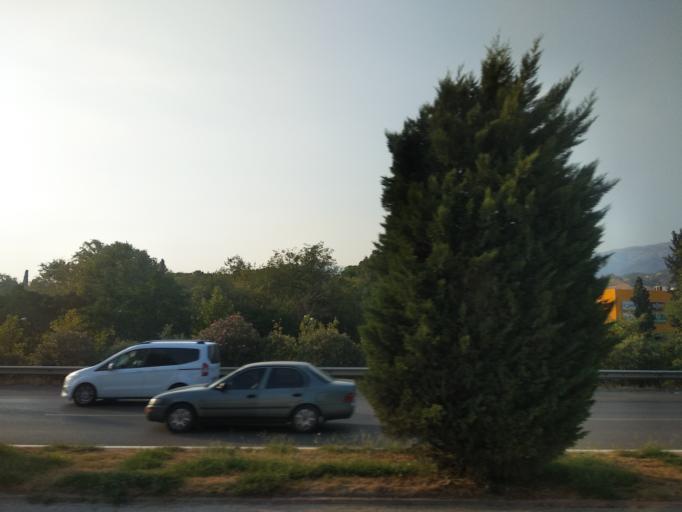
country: TR
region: Manisa
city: Salihli
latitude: 38.4846
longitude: 28.1251
